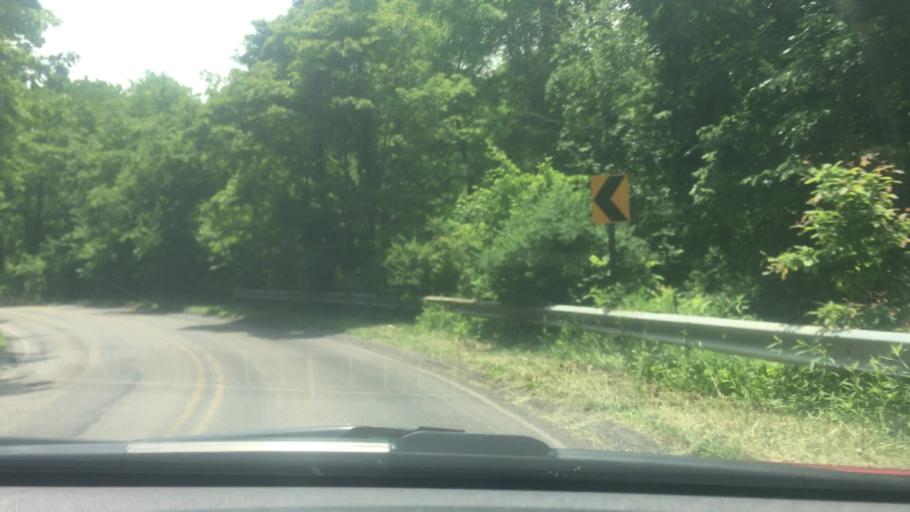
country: US
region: Pennsylvania
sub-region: Allegheny County
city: Bridgeville
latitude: 40.3432
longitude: -80.1489
